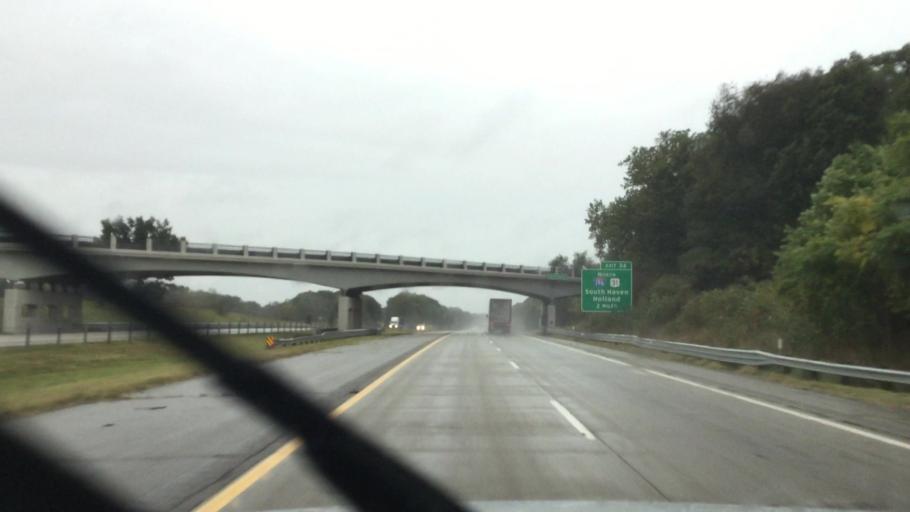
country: US
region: Michigan
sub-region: Berrien County
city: Coloma
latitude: 42.1580
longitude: -86.3355
